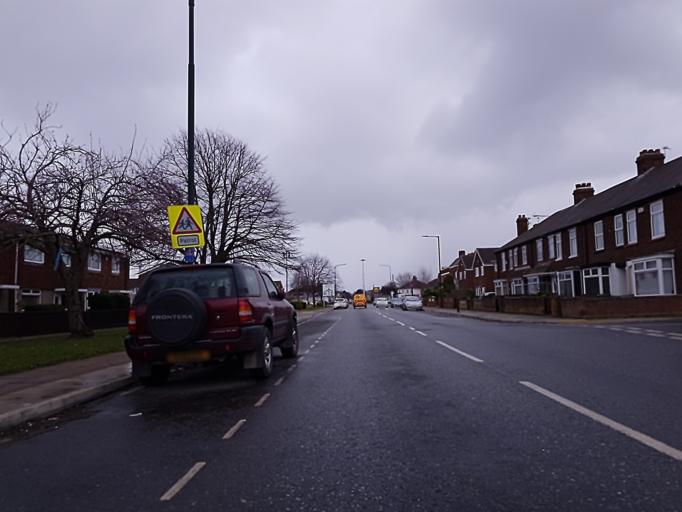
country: GB
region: England
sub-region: North East Lincolnshire
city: Grimbsy
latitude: 53.5670
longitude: -0.1057
